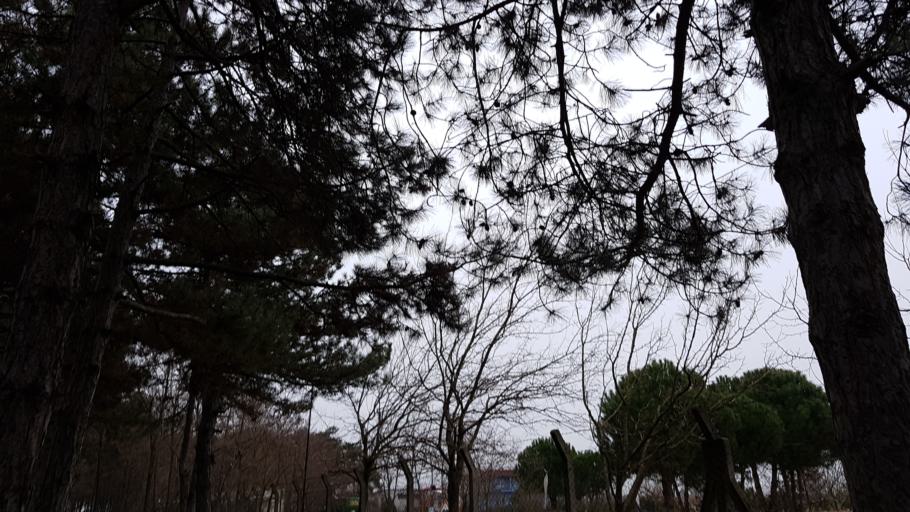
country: TR
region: Tekirdag
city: Muratli
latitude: 41.1838
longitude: 27.4770
